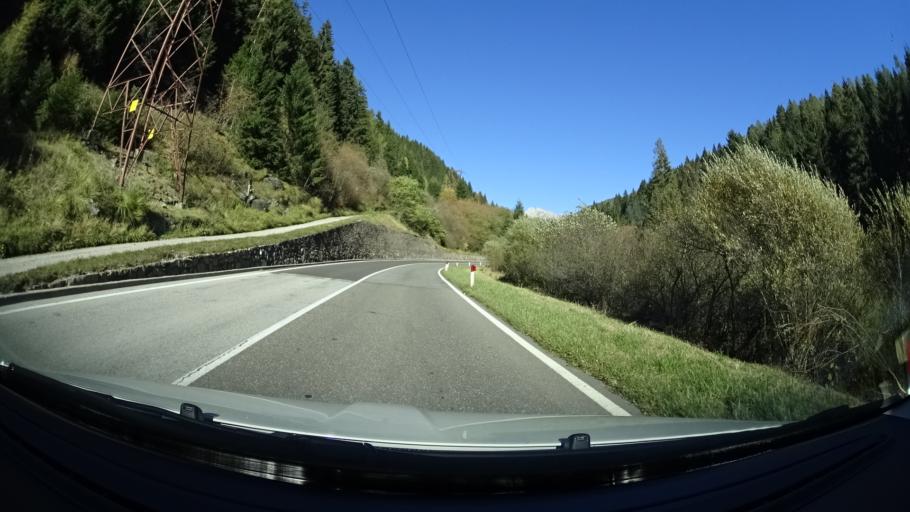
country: IT
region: Trentino-Alto Adige
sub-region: Provincia di Trento
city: Predazzo
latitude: 46.3409
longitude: 11.6130
